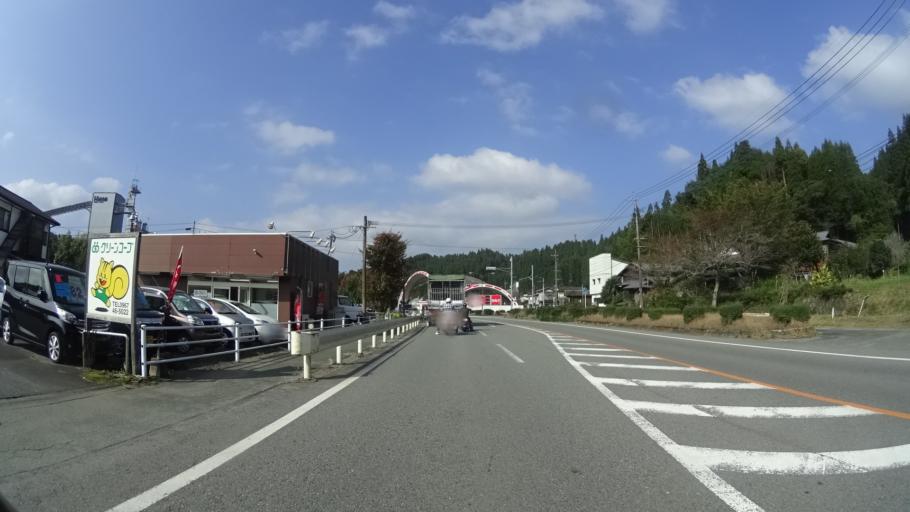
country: JP
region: Kumamoto
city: Aso
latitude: 33.1096
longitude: 131.0637
